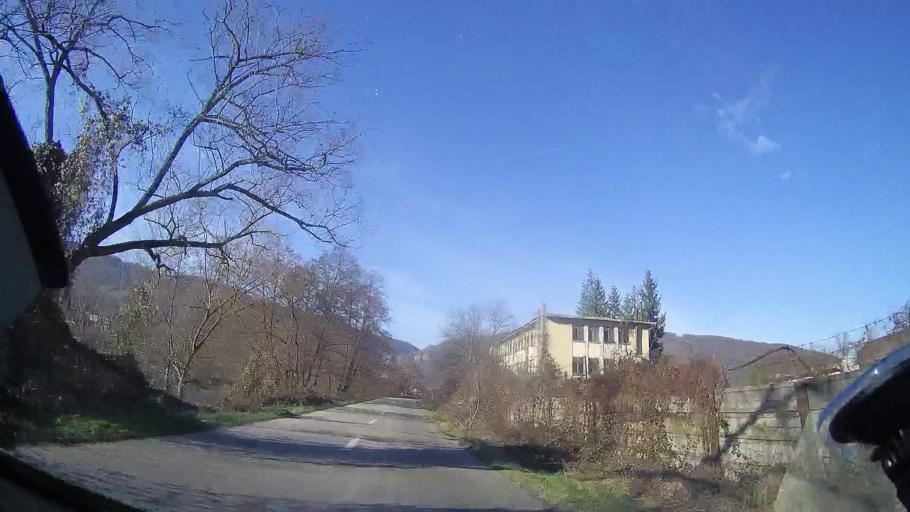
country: RO
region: Bihor
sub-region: Comuna Suncuius
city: Suncuius
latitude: 46.9465
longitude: 22.5391
